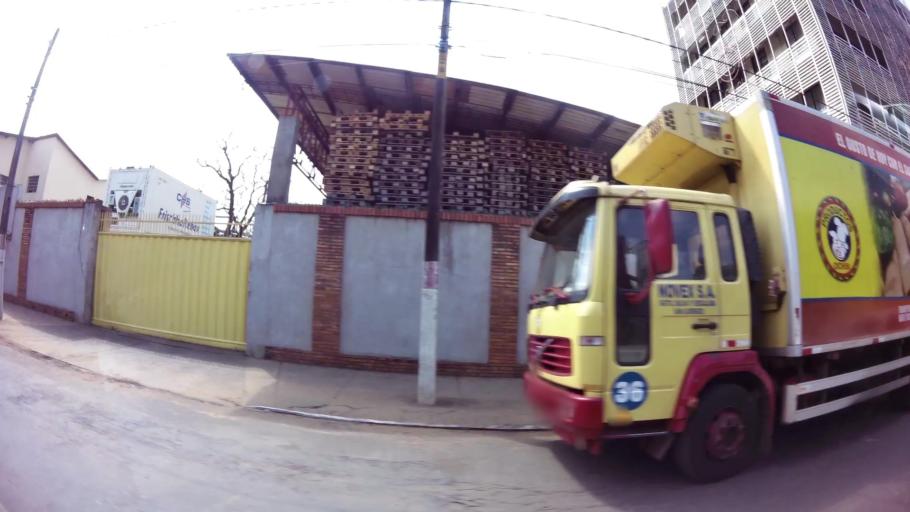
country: PY
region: Central
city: San Lorenzo
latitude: -25.3408
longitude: -57.5140
